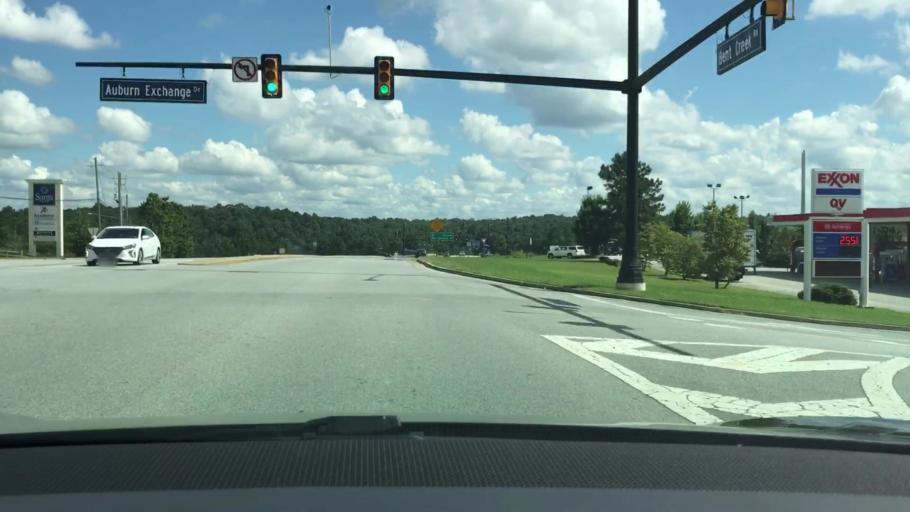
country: US
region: Alabama
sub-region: Lee County
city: Auburn
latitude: 32.6078
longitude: -85.4303
